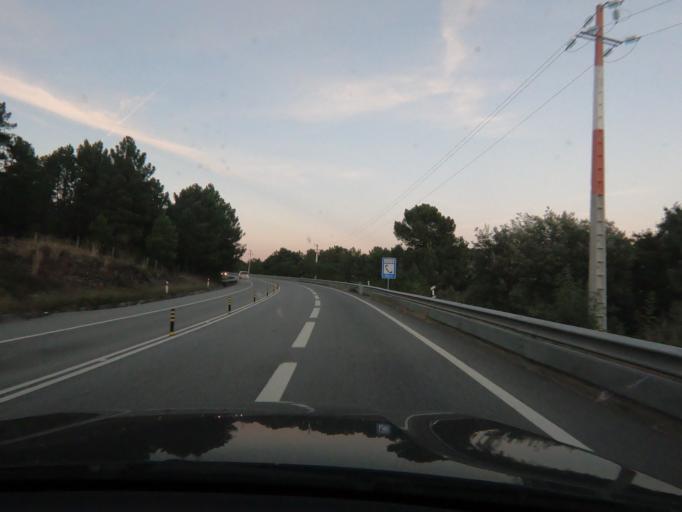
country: PT
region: Vila Real
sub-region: Vila Real
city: Vila Real
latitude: 41.3167
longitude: -7.7067
